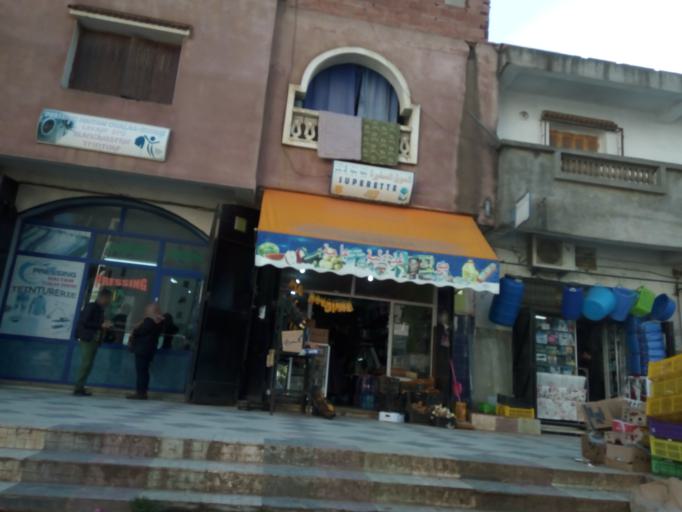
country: DZ
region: Tipaza
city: Saoula
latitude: 36.7295
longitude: 3.0034
